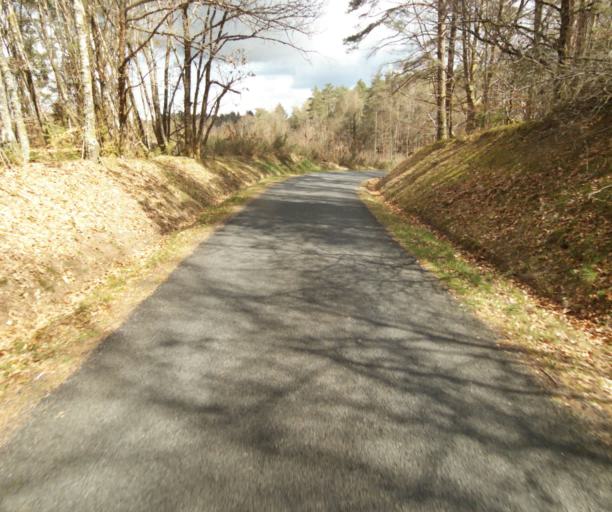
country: FR
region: Limousin
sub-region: Departement de la Correze
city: Correze
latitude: 45.2788
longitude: 1.8985
